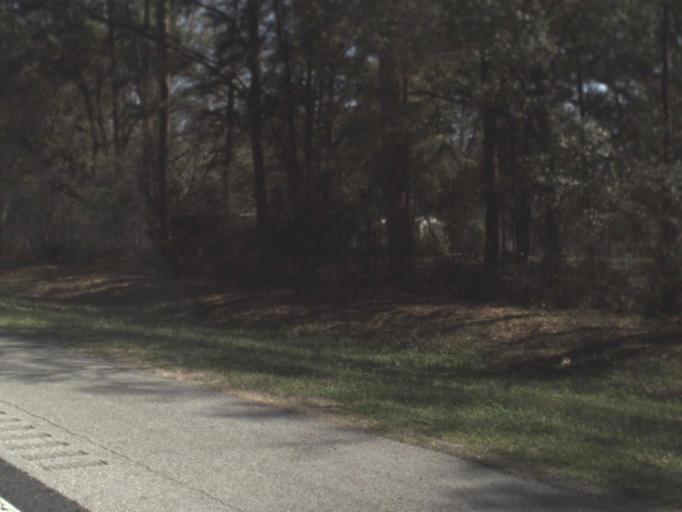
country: US
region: Florida
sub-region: Holmes County
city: Bonifay
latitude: 30.7618
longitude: -85.7174
